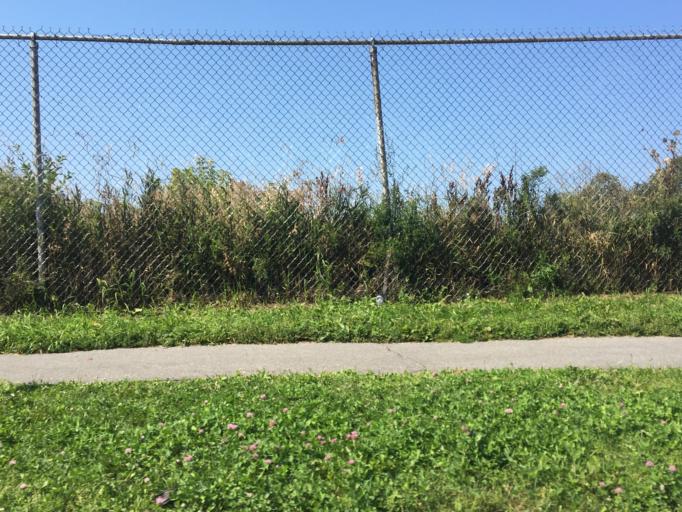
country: CA
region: Ontario
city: Ottawa
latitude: 45.3767
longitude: -75.6443
